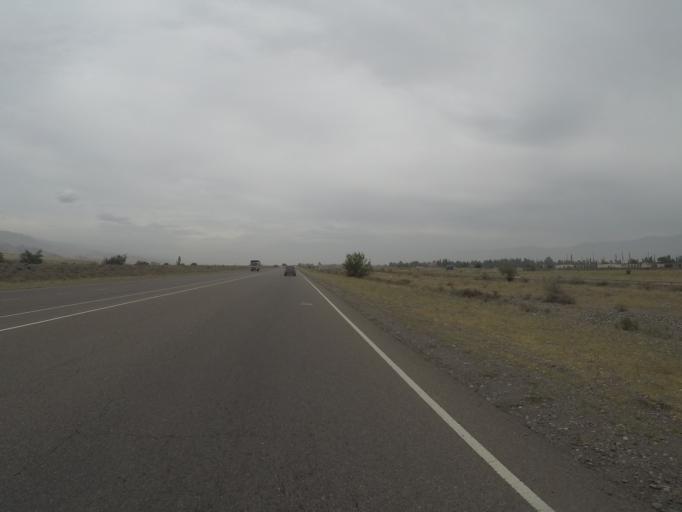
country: KG
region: Chuy
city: Bystrovka
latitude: 42.8296
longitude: 75.5216
